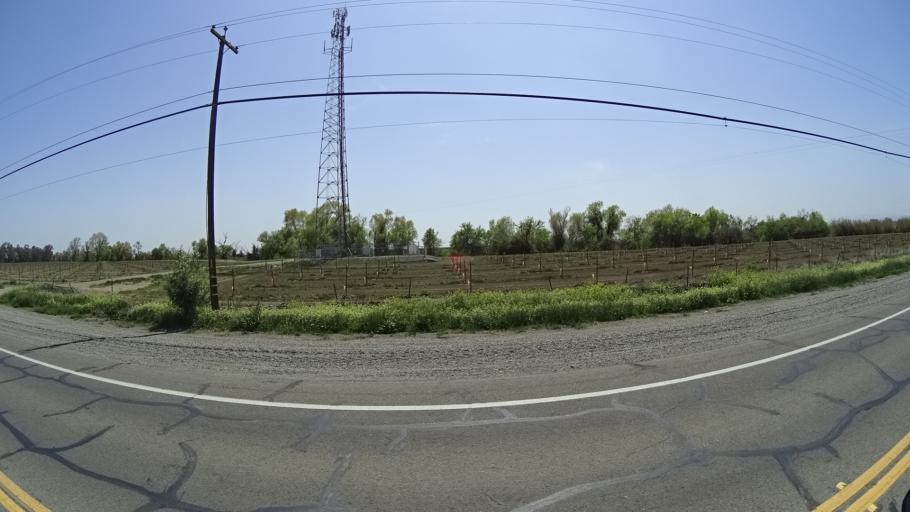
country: US
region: California
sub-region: Glenn County
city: Willows
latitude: 39.5245
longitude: -122.1698
